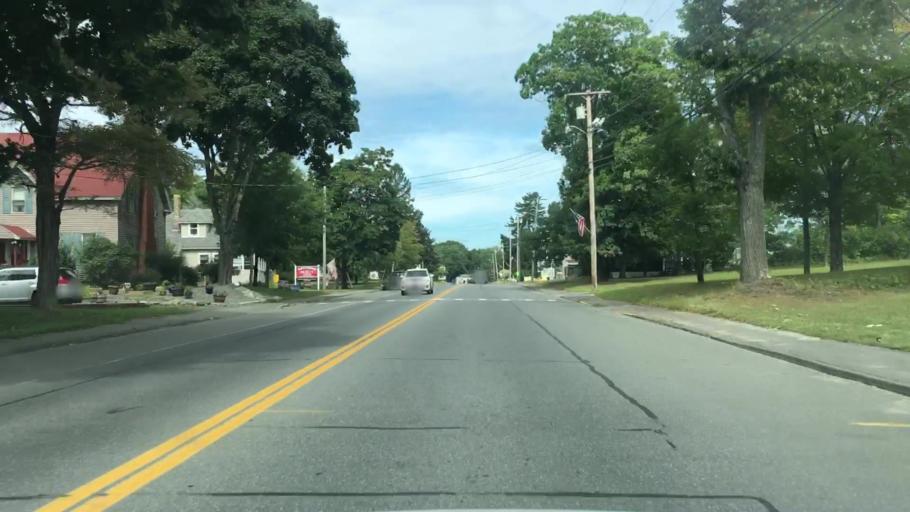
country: US
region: Maine
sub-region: Piscataquis County
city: Milo
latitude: 45.2568
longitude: -68.9871
